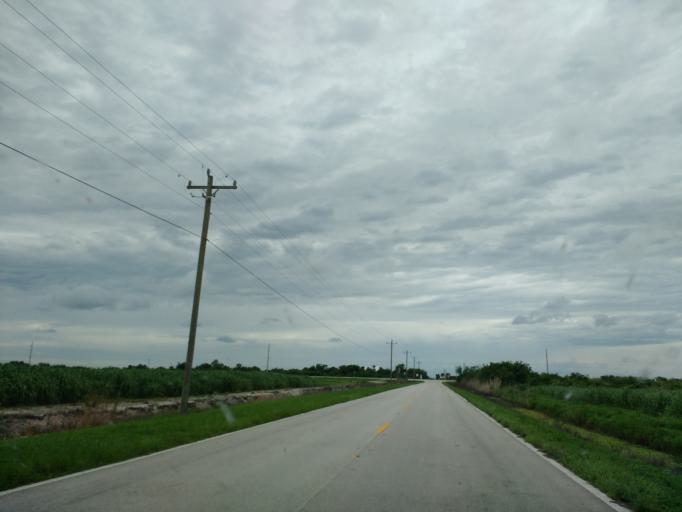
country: US
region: Florida
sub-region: Glades County
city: Moore Haven
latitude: 26.8121
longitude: -81.0796
